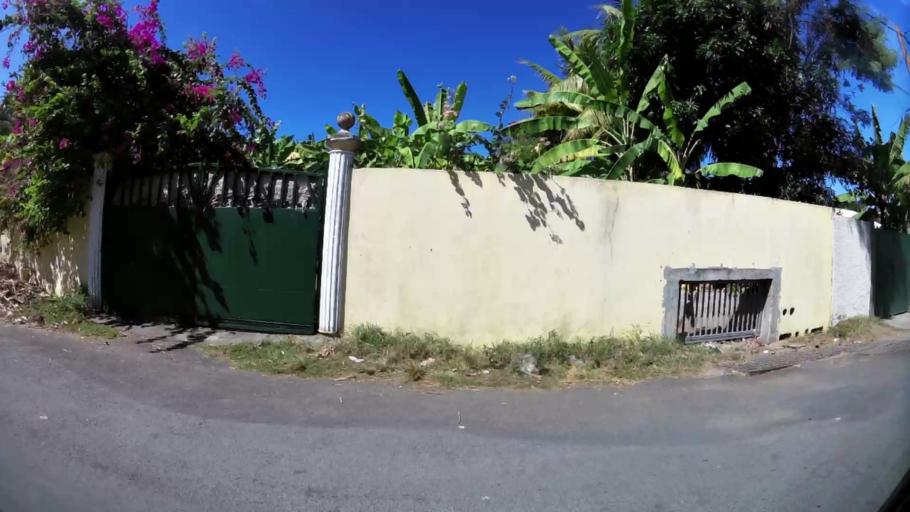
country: YT
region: Pamandzi
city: Pamandzi
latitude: -12.7954
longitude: 45.2815
